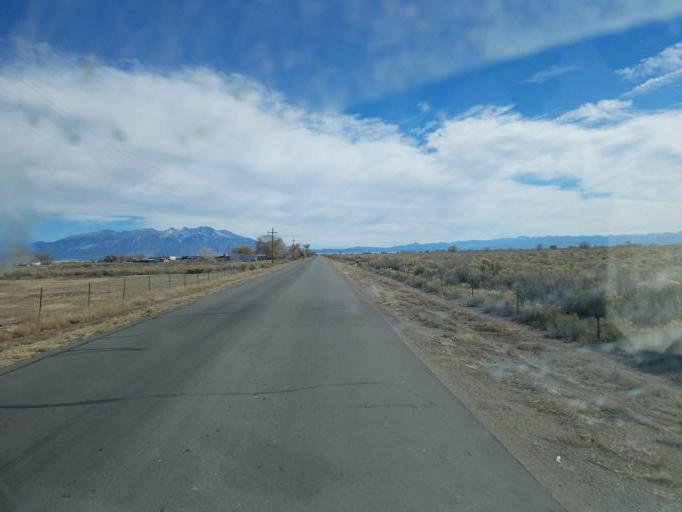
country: US
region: Colorado
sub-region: Alamosa County
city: Alamosa East
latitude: 37.5024
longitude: -105.8563
